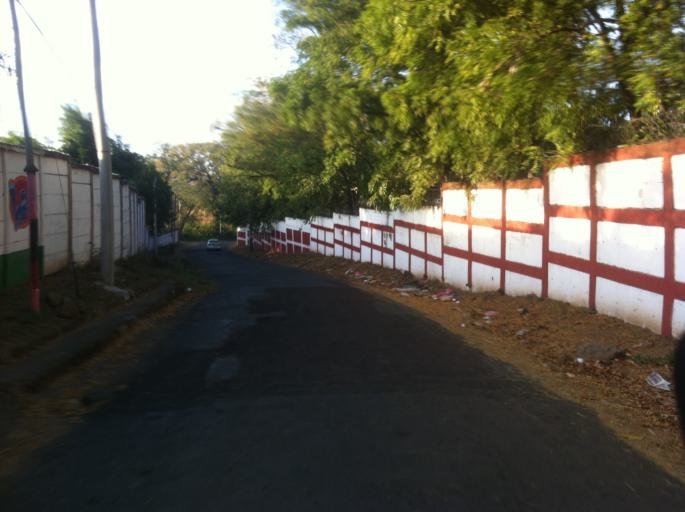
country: NI
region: Managua
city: Ciudad Sandino
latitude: 12.1046
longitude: -86.3125
